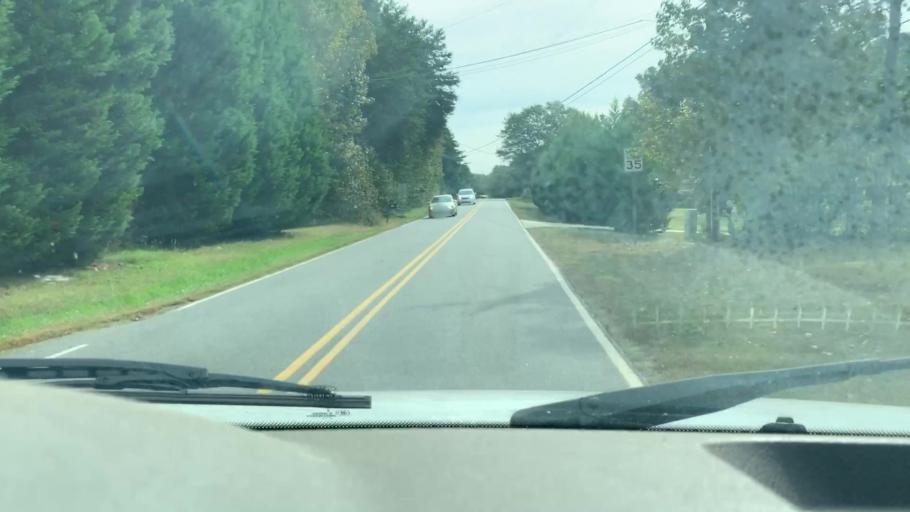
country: US
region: North Carolina
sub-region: Catawba County
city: Lake Norman of Catawba
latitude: 35.5633
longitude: -80.9242
